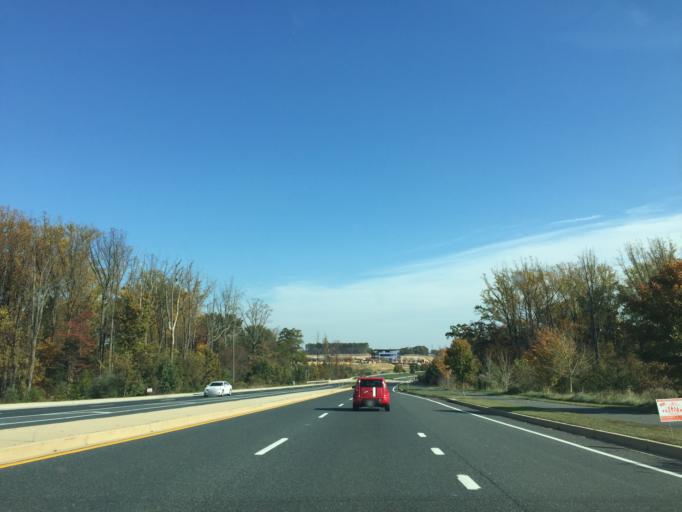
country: US
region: Maryland
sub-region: Baltimore County
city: White Marsh
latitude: 39.3613
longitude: -76.4153
